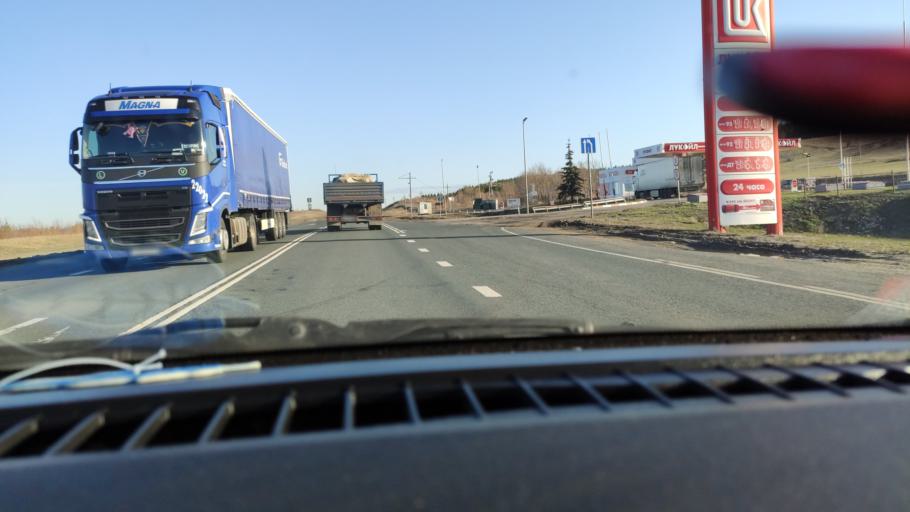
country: RU
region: Saratov
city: Alekseyevka
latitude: 52.2955
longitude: 47.9289
